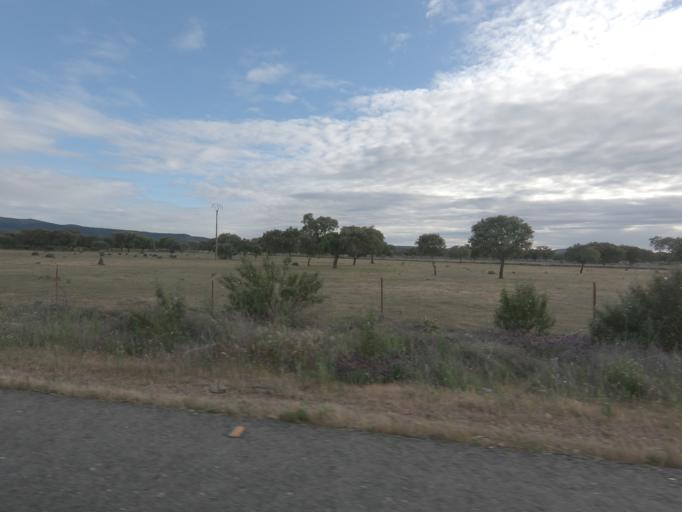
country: ES
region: Extremadura
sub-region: Provincia de Caceres
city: Torrejoncillo
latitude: 39.8768
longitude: -6.4485
